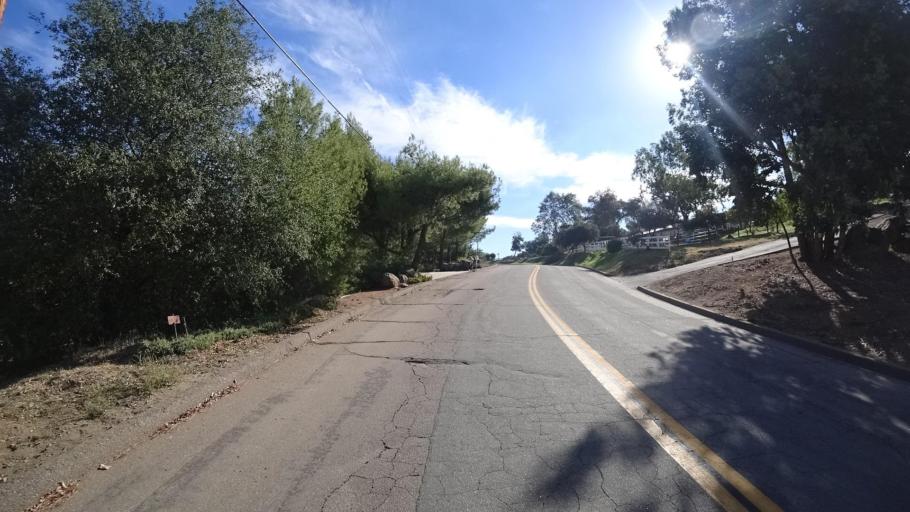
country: US
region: California
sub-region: San Diego County
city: Alpine
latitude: 32.8220
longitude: -116.7471
